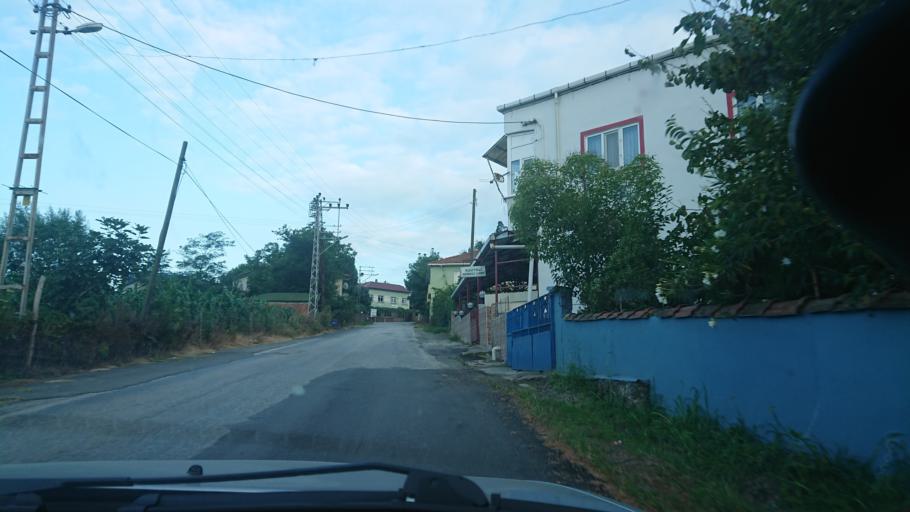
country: TR
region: Samsun
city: Tekkekoy
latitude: 41.1723
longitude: 36.5310
